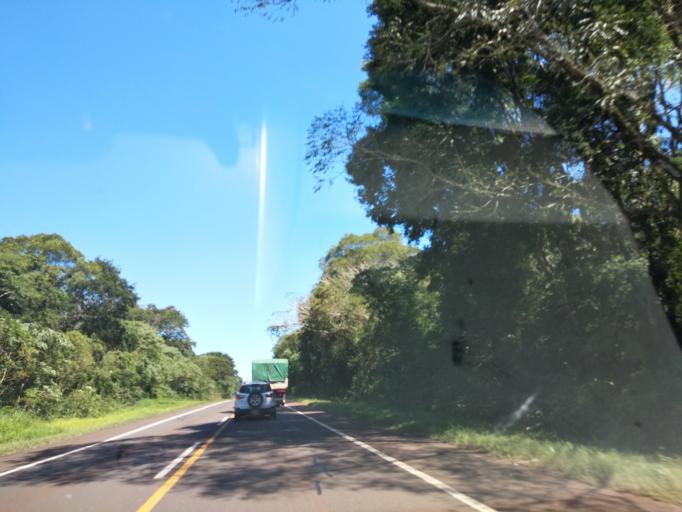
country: AR
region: Misiones
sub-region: Departamento de Iguazu
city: Puerto Iguazu
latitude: -25.7076
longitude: -54.5164
